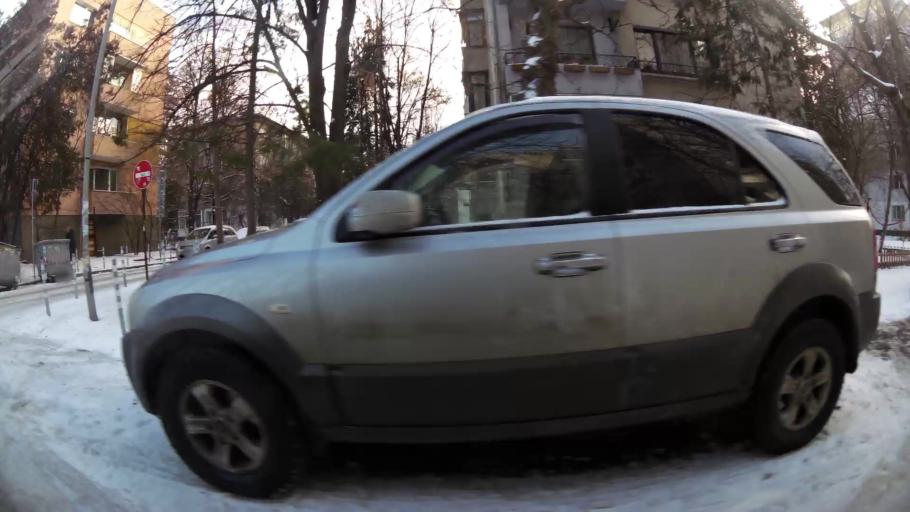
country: BG
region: Sofia-Capital
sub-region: Stolichna Obshtina
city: Sofia
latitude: 42.6689
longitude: 23.3211
